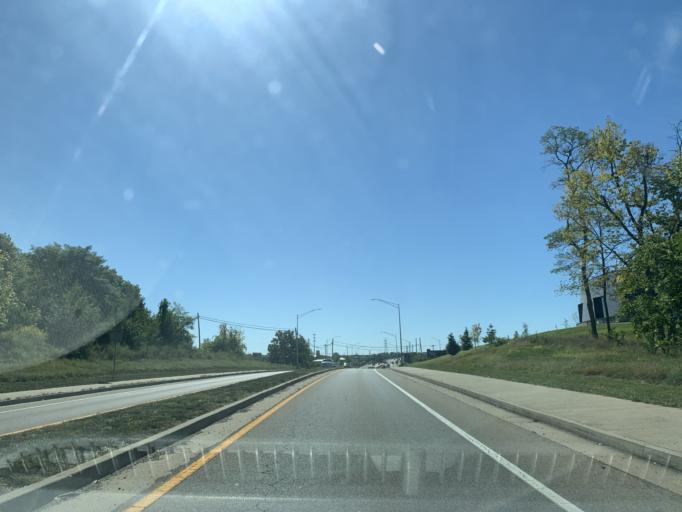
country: US
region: Kentucky
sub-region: Boone County
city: Francisville
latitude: 39.0948
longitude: -84.7150
